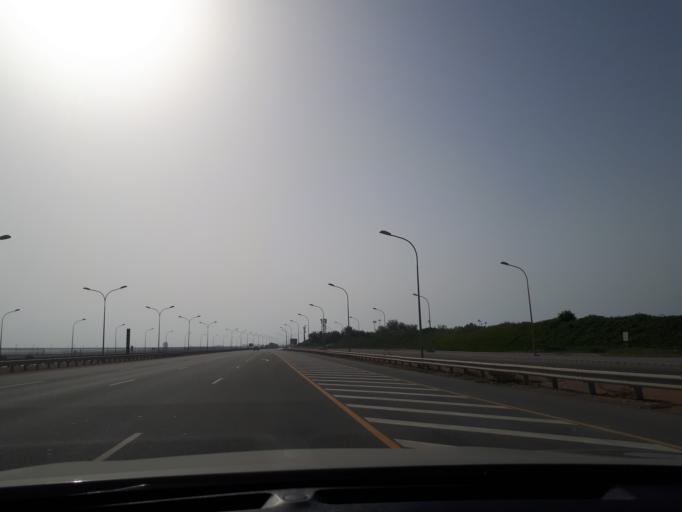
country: OM
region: Muhafazat Masqat
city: Bawshar
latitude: 23.6105
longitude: 58.3045
